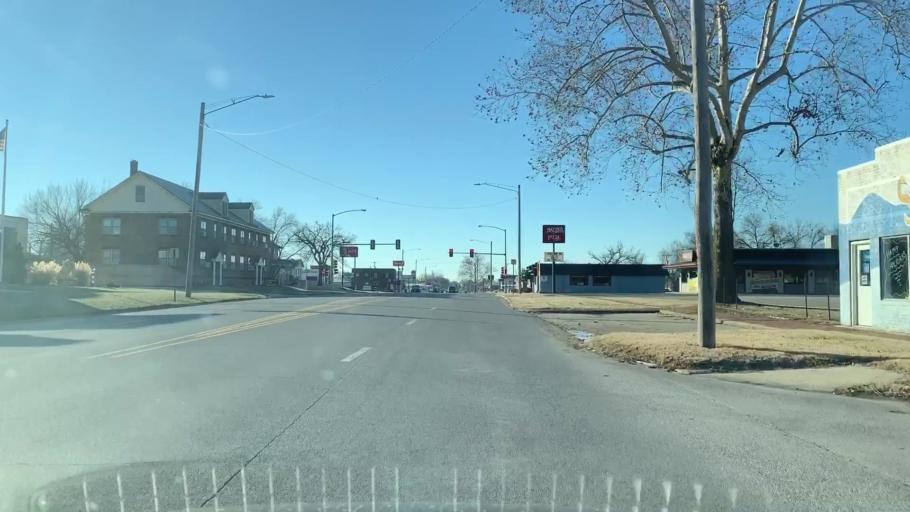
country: US
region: Kansas
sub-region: Crawford County
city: Pittsburg
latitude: 37.4013
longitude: -94.7050
